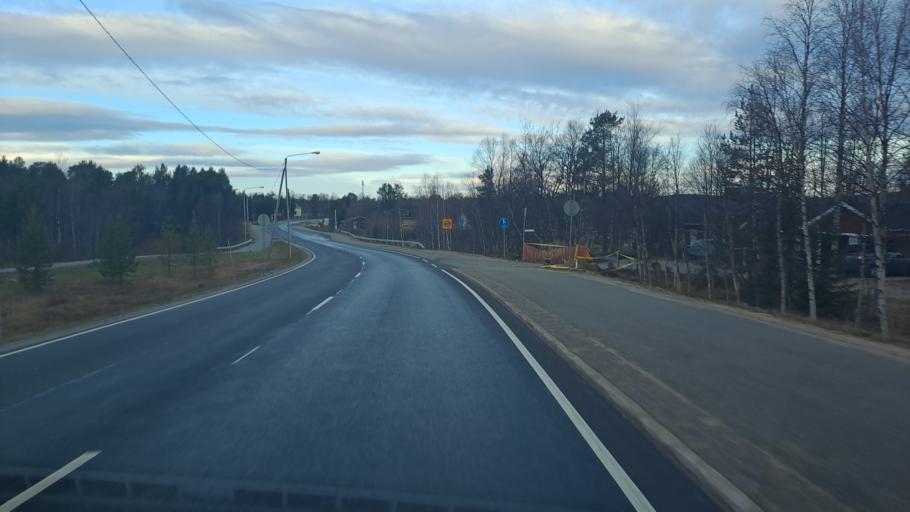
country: FI
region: Lapland
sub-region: Pohjois-Lappi
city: Inari
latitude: 68.9013
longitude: 27.0424
